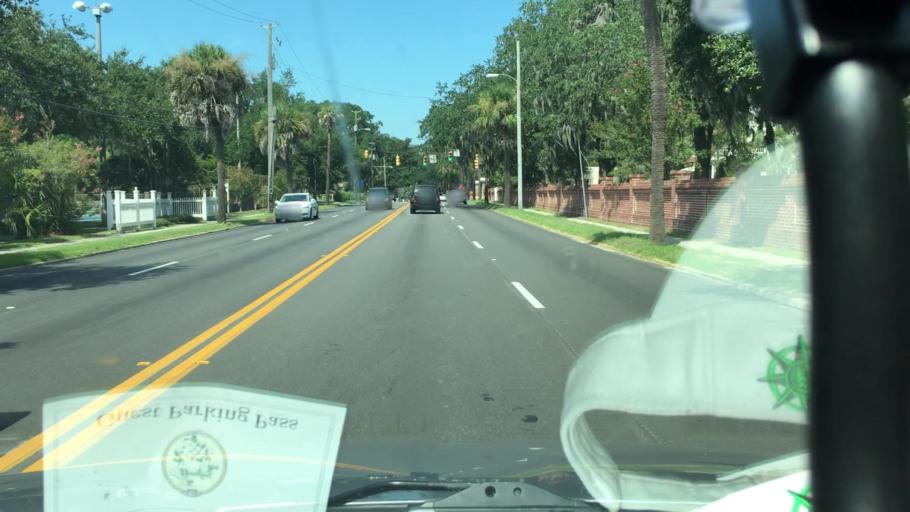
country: US
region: South Carolina
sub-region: Beaufort County
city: Beaufort
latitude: 32.4397
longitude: -80.6785
